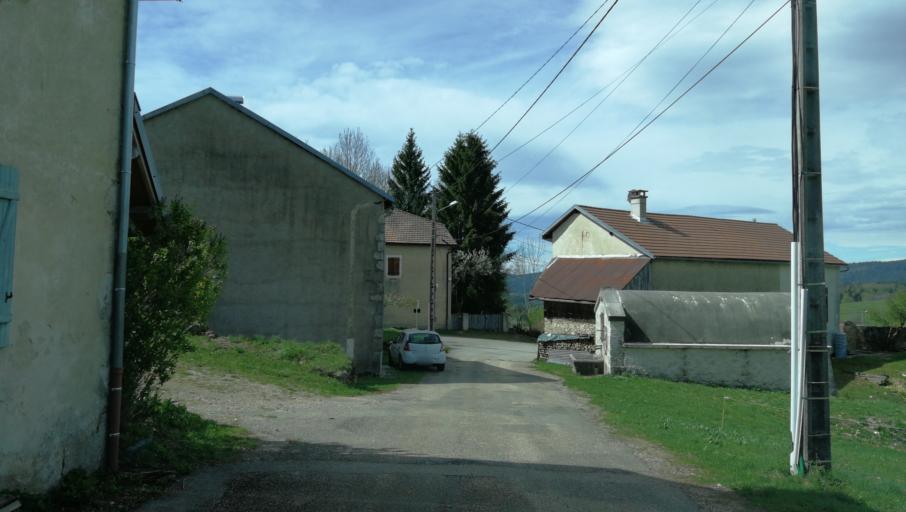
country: FR
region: Rhone-Alpes
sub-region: Departement de l'Ain
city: Chatillon-en-Michaille
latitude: 46.2547
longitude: 5.7875
